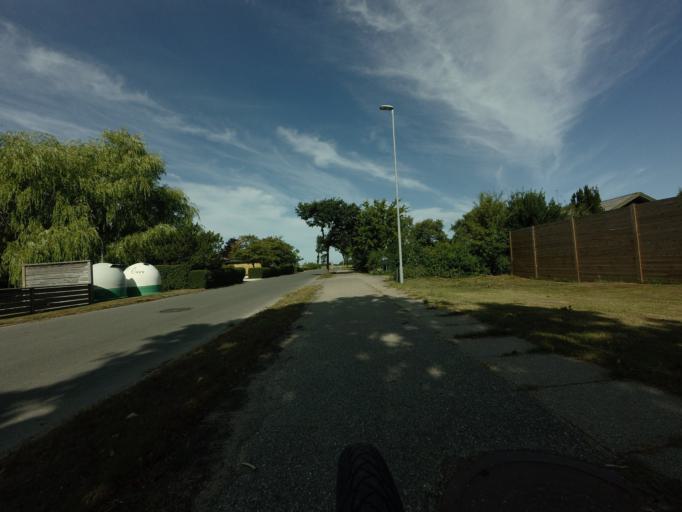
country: DK
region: North Denmark
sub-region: Hjorring Kommune
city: Vra
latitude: 57.4055
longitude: 9.9225
